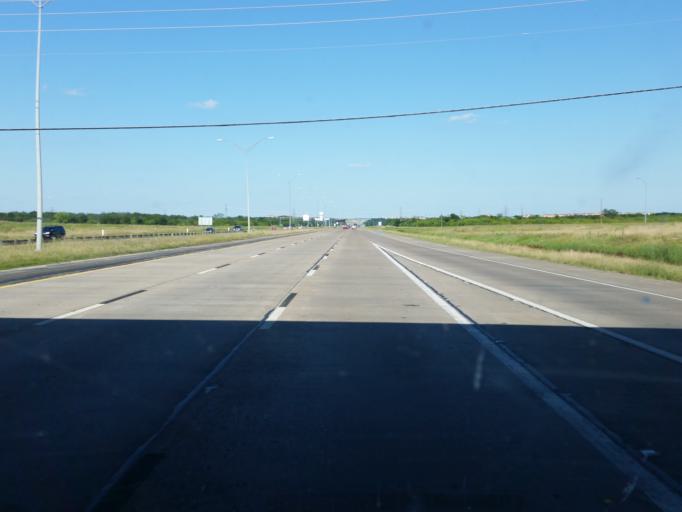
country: US
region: Texas
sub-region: Tarrant County
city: Benbrook
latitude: 32.6839
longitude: -97.4523
